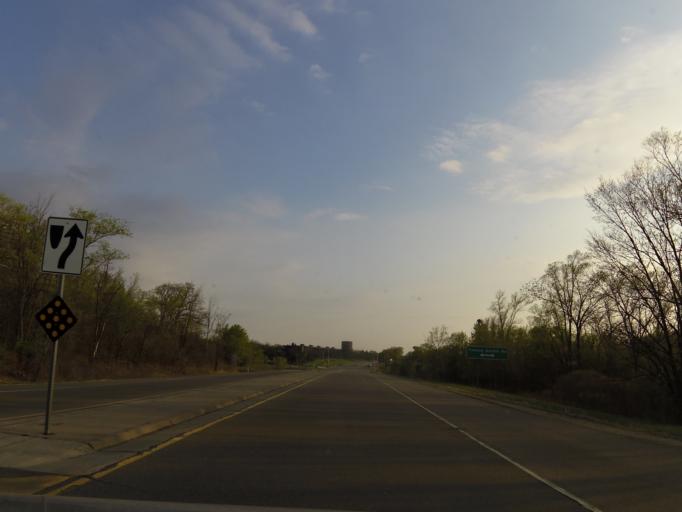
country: US
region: Minnesota
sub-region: Dakota County
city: Eagan
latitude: 44.8367
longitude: -93.1893
